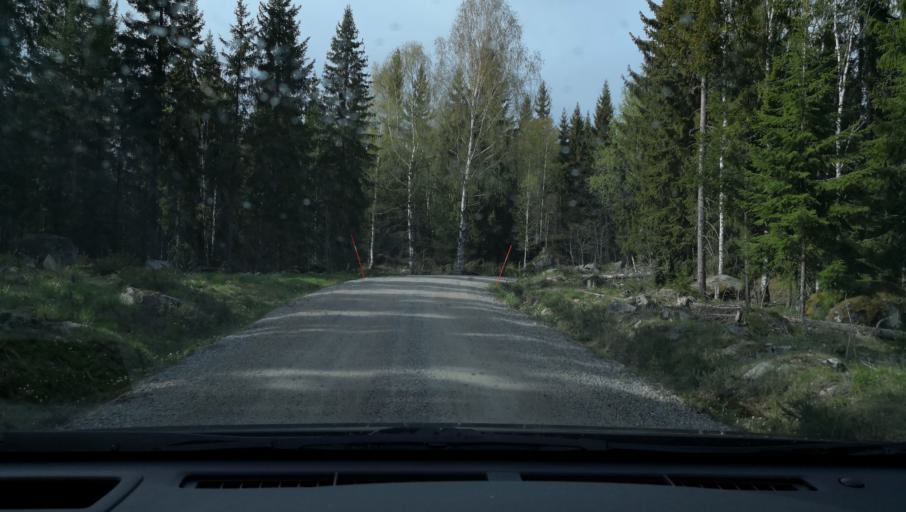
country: SE
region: Vaestmanland
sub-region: Fagersta Kommun
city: Fagersta
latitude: 60.1566
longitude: 15.6973
